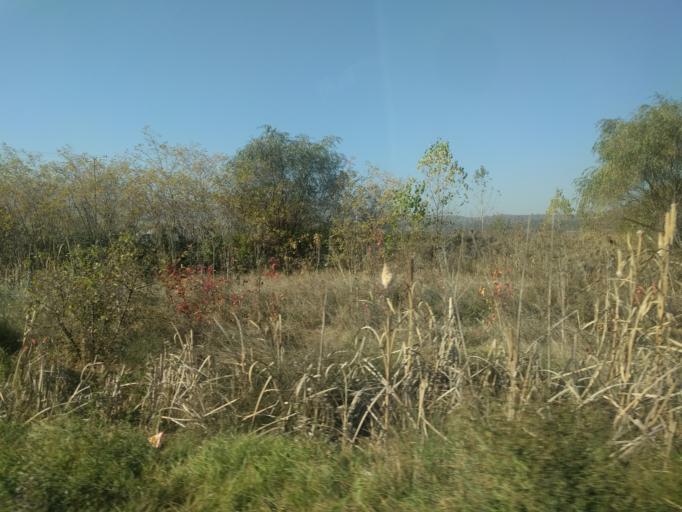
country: XK
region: Pristina
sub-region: Komuna e Gracanices
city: Glanica
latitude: 42.5884
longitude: 21.0172
